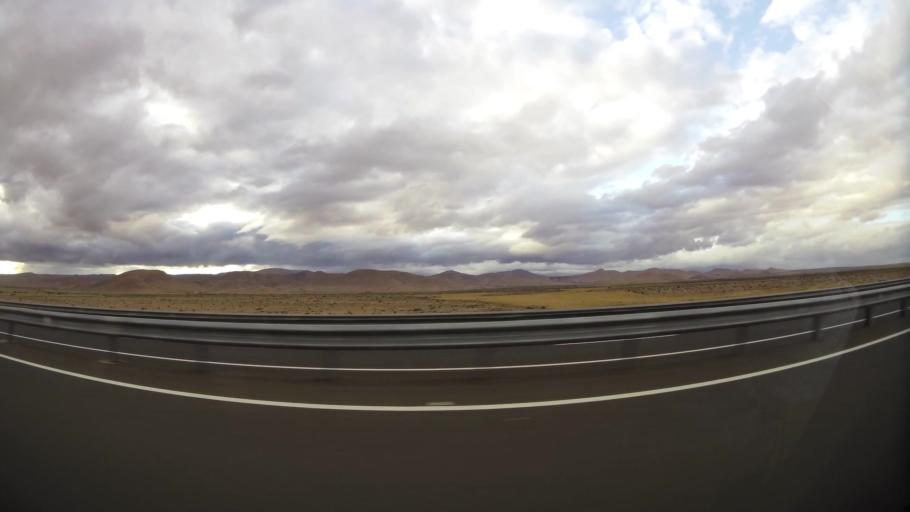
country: MA
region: Taza-Al Hoceima-Taounate
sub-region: Taza
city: Guercif
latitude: 34.3271
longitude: -3.5517
